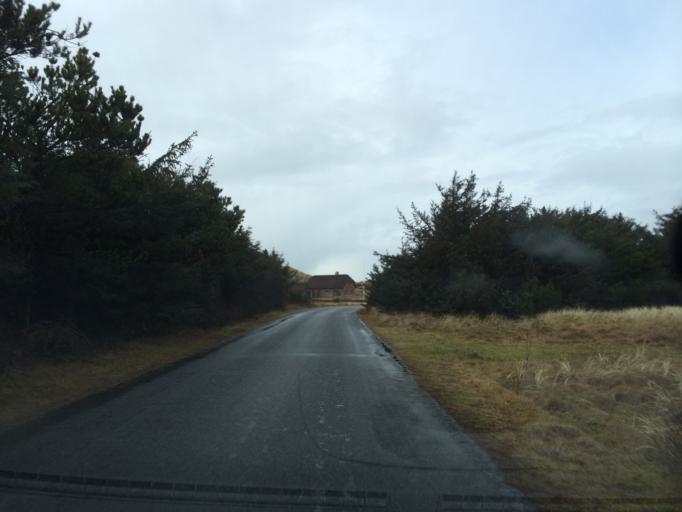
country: DK
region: Central Jutland
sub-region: Holstebro Kommune
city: Ulfborg
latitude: 56.2493
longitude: 8.1361
